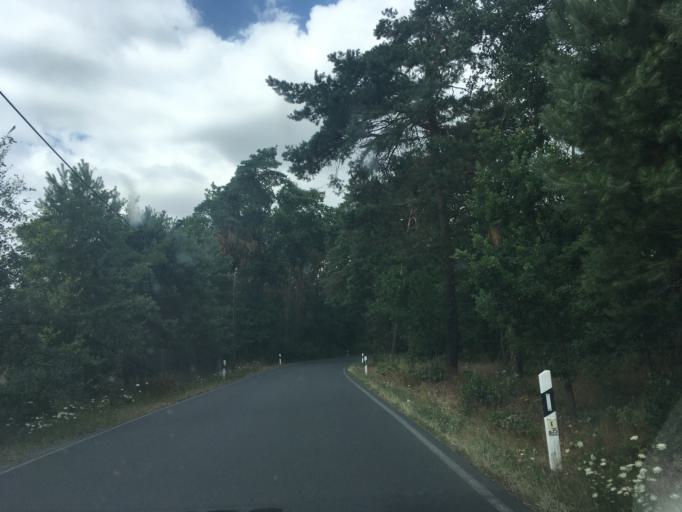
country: DE
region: Saxony
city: Thiendorf
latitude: 51.2817
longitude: 13.7373
